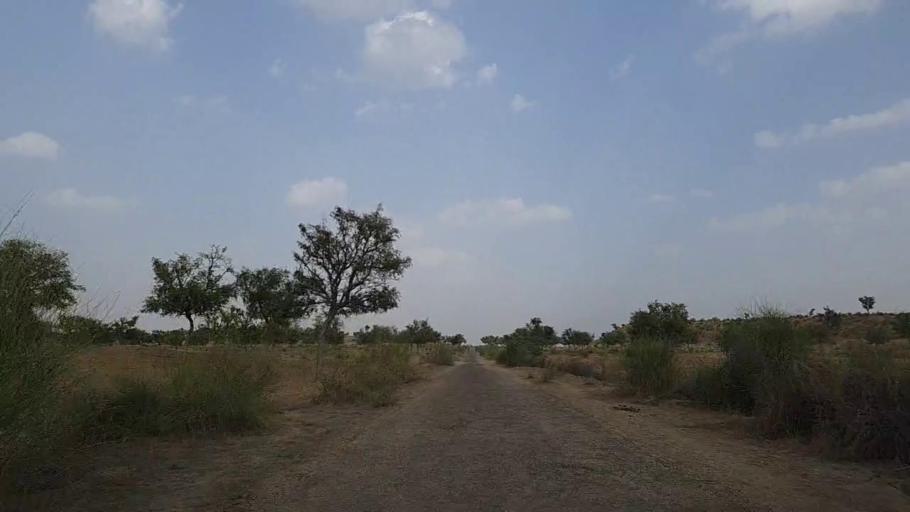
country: PK
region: Sindh
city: Islamkot
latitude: 24.7682
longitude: 70.1615
